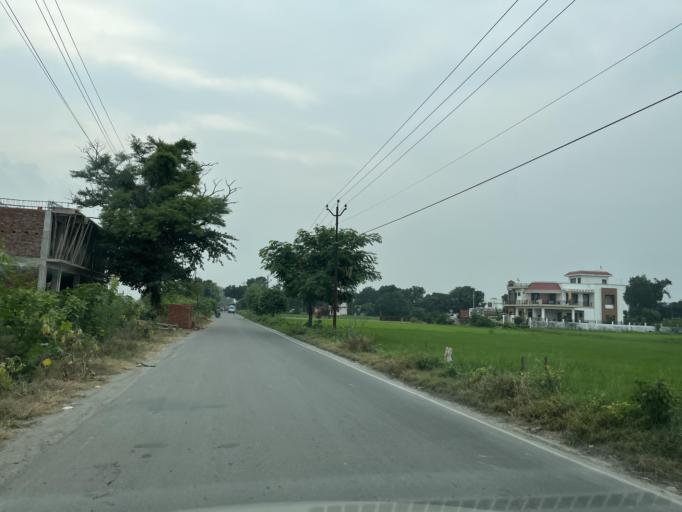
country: IN
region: Uttarakhand
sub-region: Naini Tal
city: Haldwani
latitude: 29.1729
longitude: 79.4858
